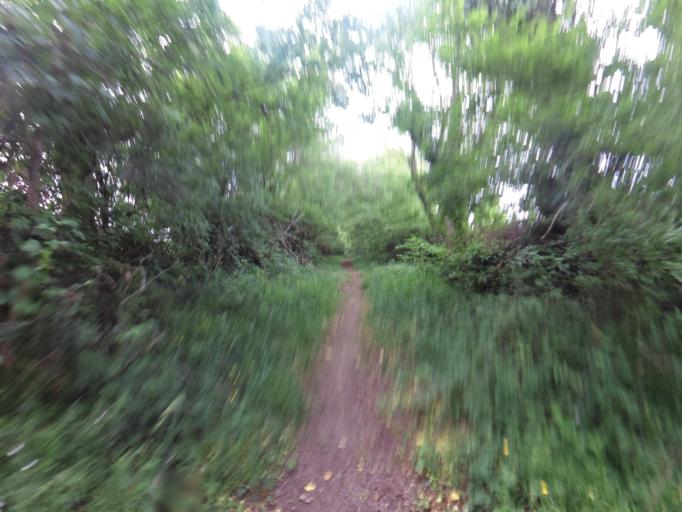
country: FR
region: Brittany
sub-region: Departement du Morbihan
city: Molac
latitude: 47.7648
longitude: -2.4316
